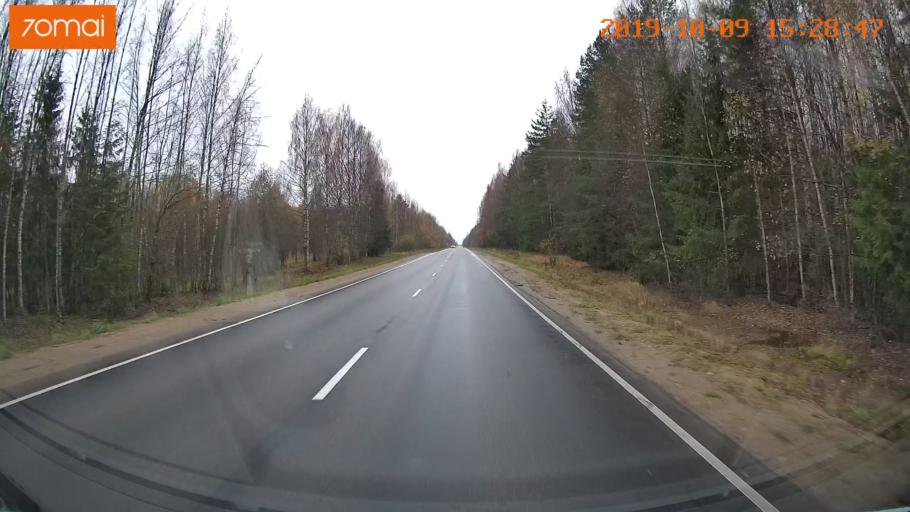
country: RU
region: Kostroma
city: Susanino
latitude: 57.9990
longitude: 41.3540
